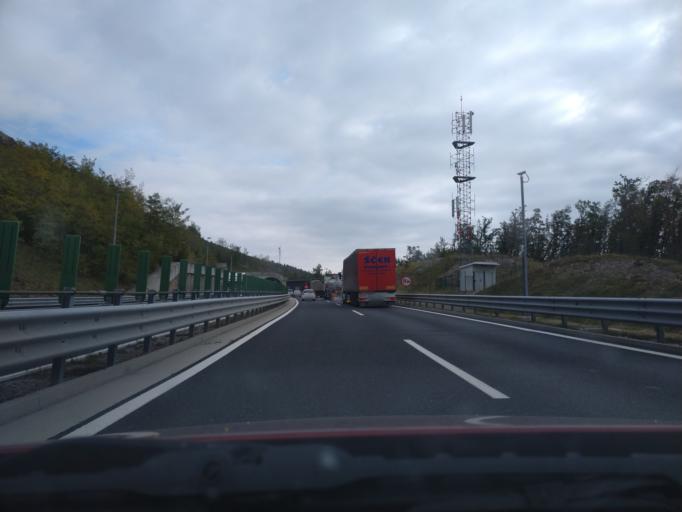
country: SI
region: Vipava
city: Vipava
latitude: 45.7738
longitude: 14.0232
